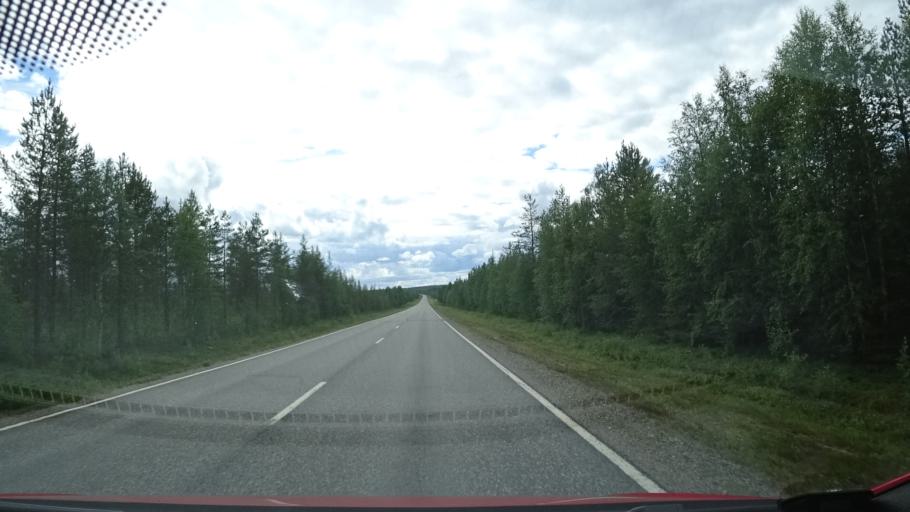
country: FI
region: Lapland
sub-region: Tunturi-Lappi
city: Kittilae
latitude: 67.5493
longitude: 24.9187
